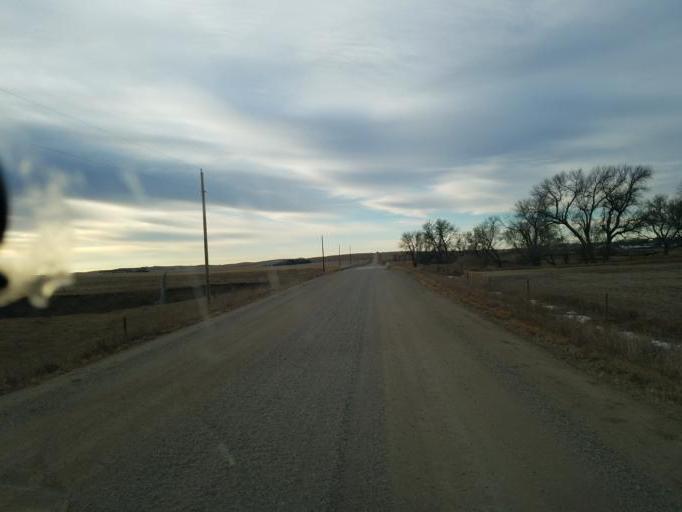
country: US
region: Nebraska
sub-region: Knox County
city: Bloomfield
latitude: 42.5711
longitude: -97.6819
